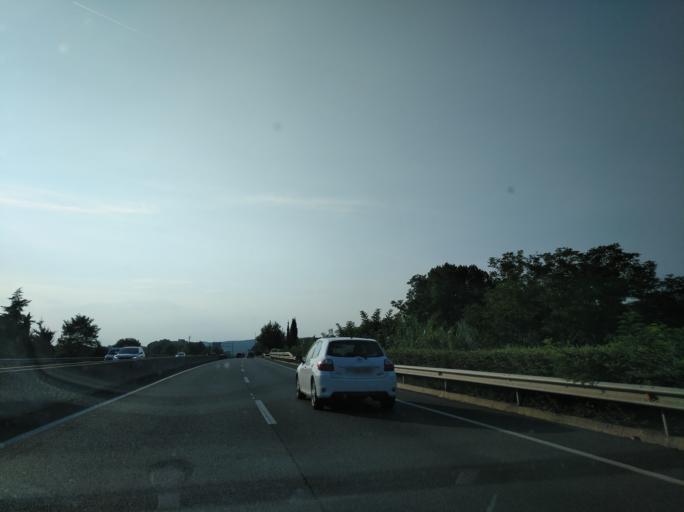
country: ES
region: Catalonia
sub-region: Provincia de Girona
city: Santa Cristina d'Aro
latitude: 41.8102
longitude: 2.9953
